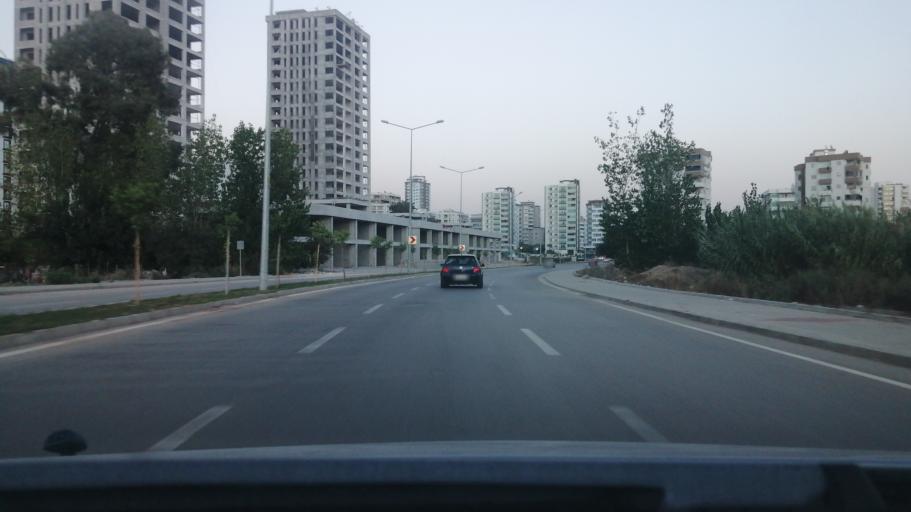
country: TR
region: Adana
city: Seyhan
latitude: 37.0159
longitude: 35.2598
